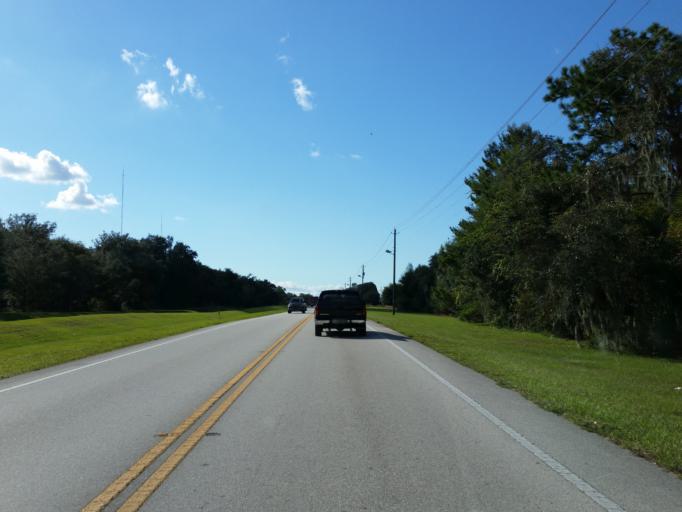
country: US
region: Florida
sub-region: Hillsborough County
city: Fish Hawk
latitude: 27.8541
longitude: -82.2371
